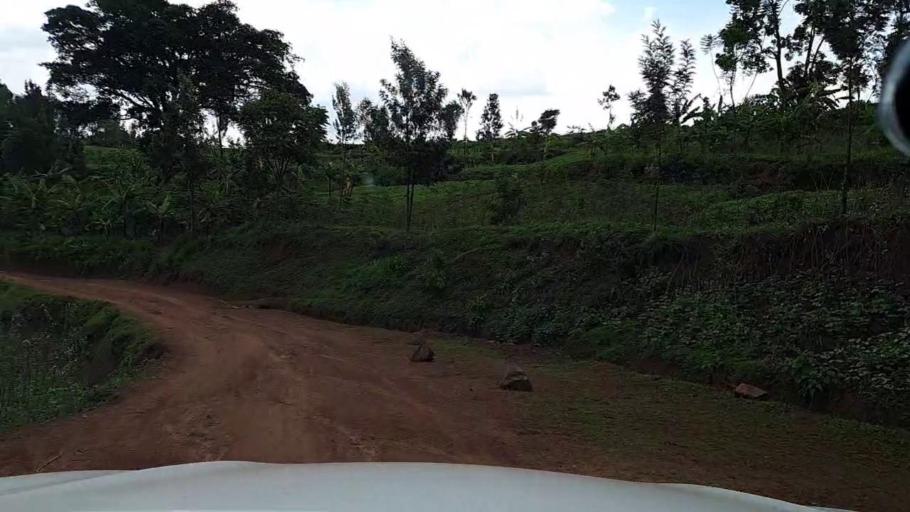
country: RW
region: Southern Province
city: Butare
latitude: -2.7559
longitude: 29.7464
